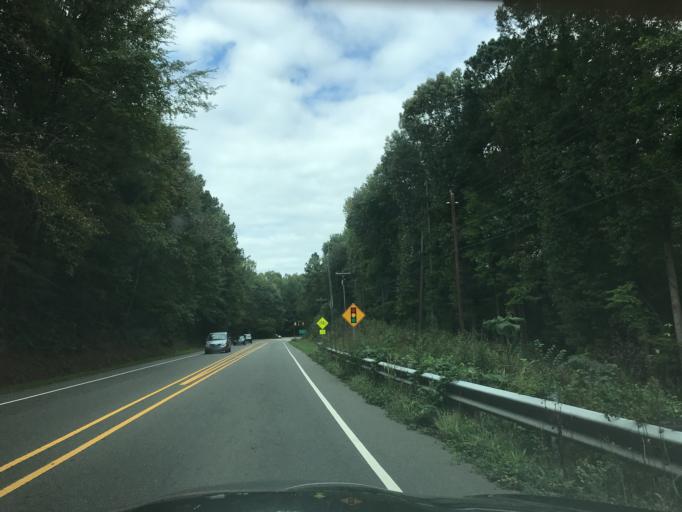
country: US
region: North Carolina
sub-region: Orange County
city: Chapel Hill
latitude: 35.9269
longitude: -79.0678
